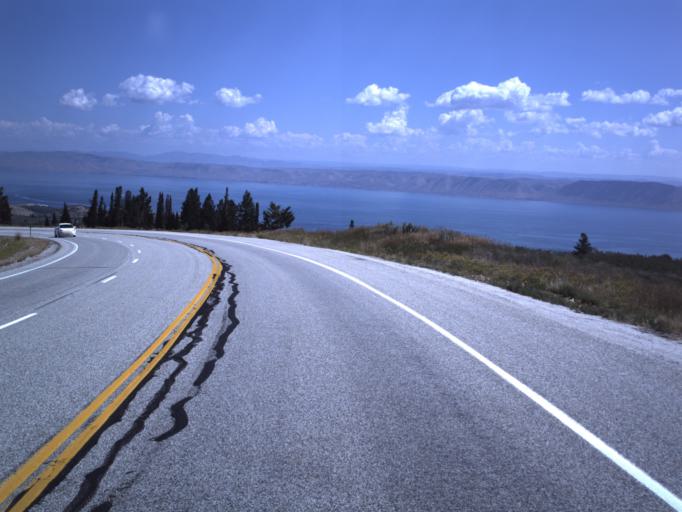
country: US
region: Idaho
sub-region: Bear Lake County
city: Paris
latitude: 41.9283
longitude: -111.4507
